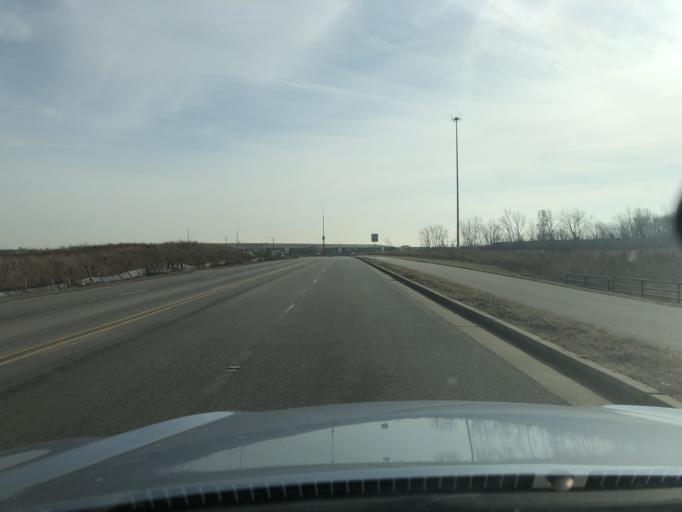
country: US
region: Illinois
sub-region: DuPage County
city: Bensenville
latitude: 41.9779
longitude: -87.9426
